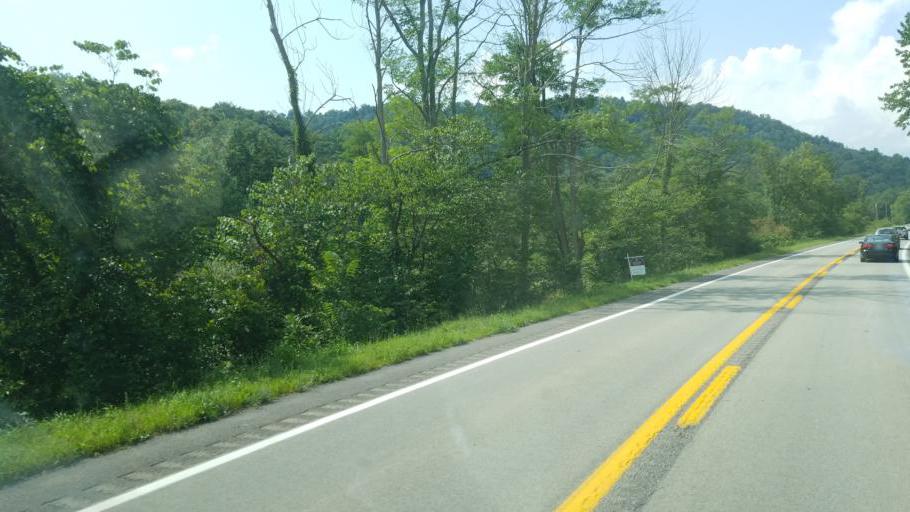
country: US
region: Virginia
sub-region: Frederick County
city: Shawnee Land
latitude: 39.3892
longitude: -78.3763
